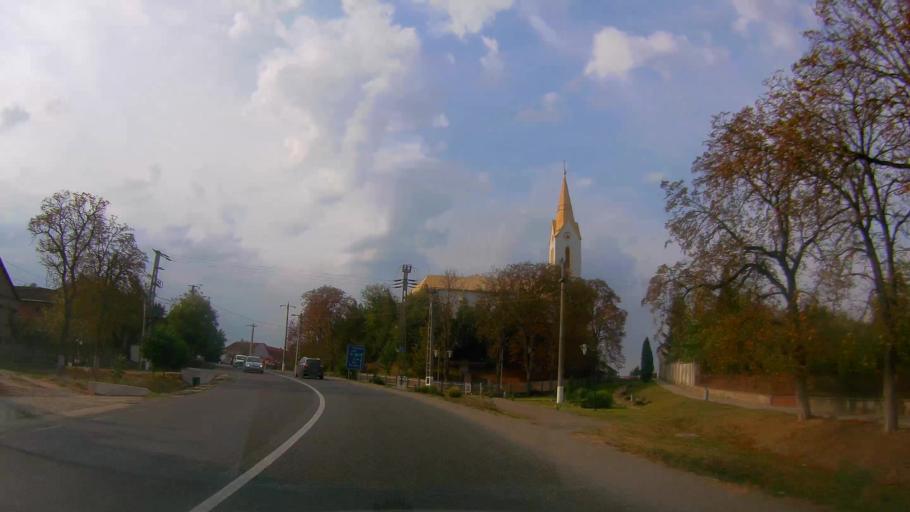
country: RO
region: Satu Mare
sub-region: Oras Ardud
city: Ardud
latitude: 47.6389
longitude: 22.8875
